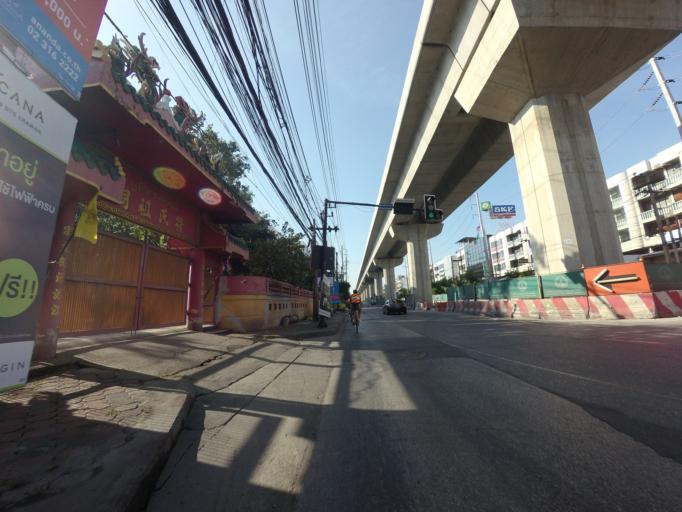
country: TH
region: Samut Prakan
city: Samut Prakan
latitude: 13.6427
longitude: 100.5944
